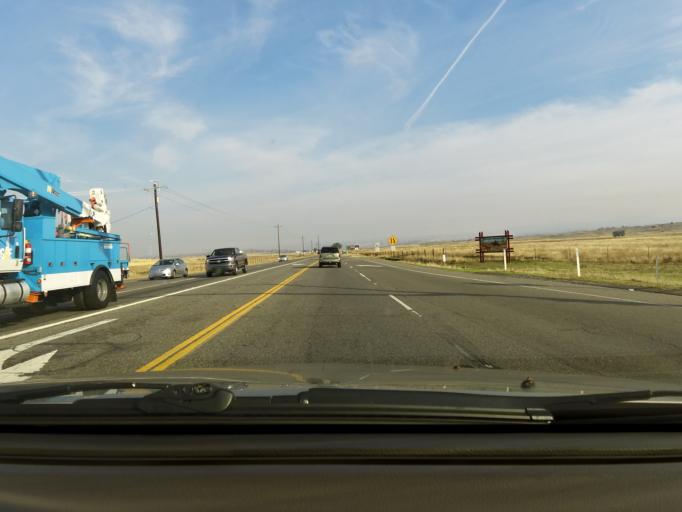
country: US
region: California
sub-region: Madera County
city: Bonadelle Ranchos-Madera Ranchos
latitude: 37.0105
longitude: -119.7939
